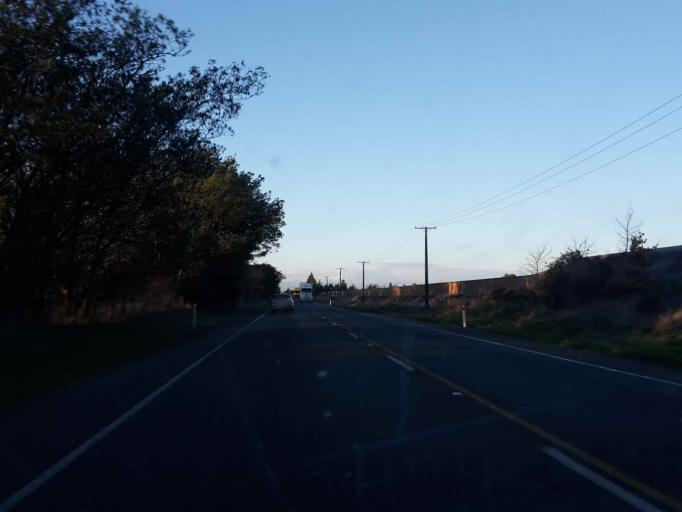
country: NZ
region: Canterbury
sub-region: Selwyn District
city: Rolleston
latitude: -43.6003
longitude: 172.3541
